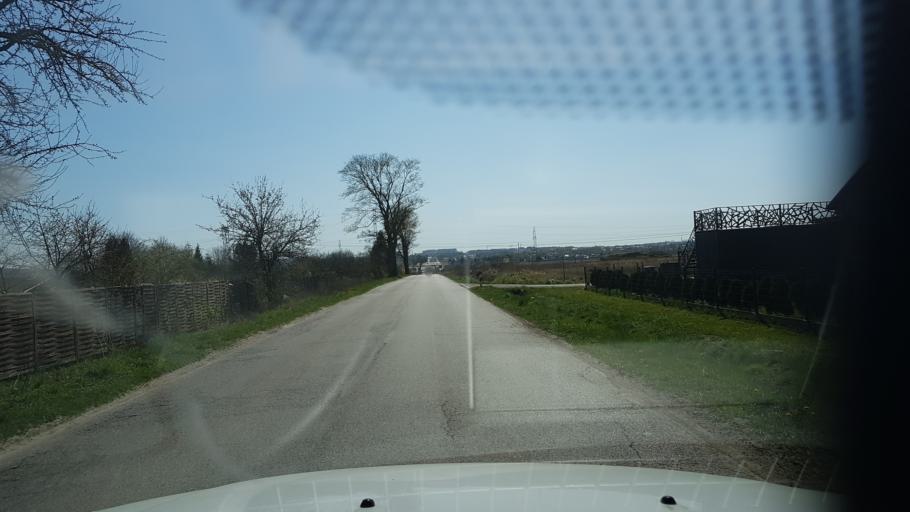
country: PL
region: West Pomeranian Voivodeship
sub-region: Koszalin
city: Koszalin
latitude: 54.2380
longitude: 16.1771
